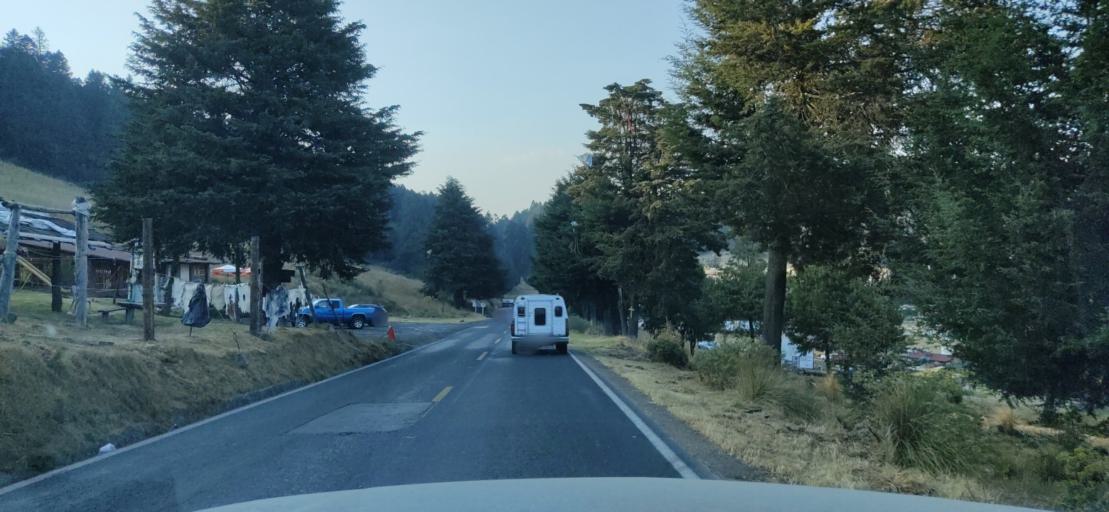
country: MX
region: Mexico
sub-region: Ocoyoacac
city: San Jeronimo Acazulco
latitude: 19.2774
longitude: -99.3801
